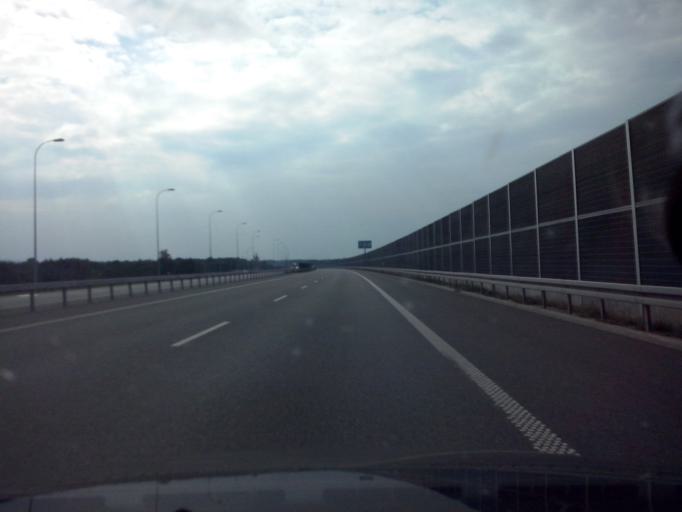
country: PL
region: Lesser Poland Voivodeship
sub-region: Powiat brzeski
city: Brzesko
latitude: 50.0000
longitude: 20.6291
